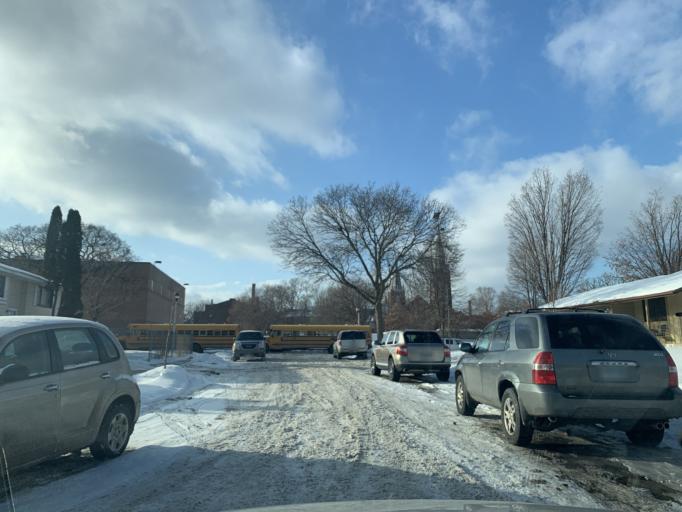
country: US
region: Minnesota
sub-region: Hennepin County
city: Minneapolis
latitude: 44.9967
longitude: -93.2889
